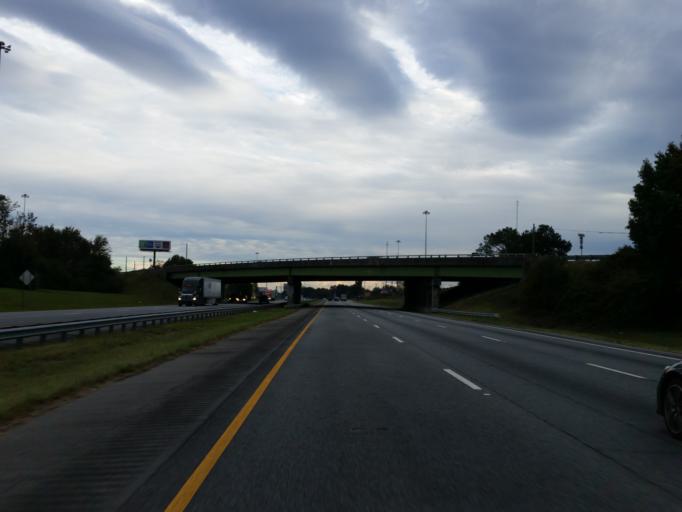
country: US
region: Georgia
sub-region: Lowndes County
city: Remerton
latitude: 30.8461
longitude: -83.3312
